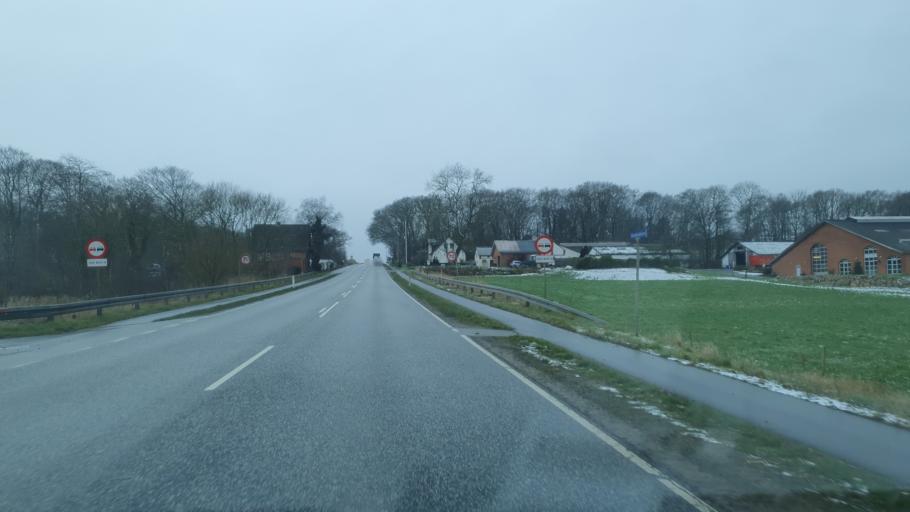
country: DK
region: North Denmark
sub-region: Jammerbugt Kommune
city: Brovst
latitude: 57.0958
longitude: 9.4974
